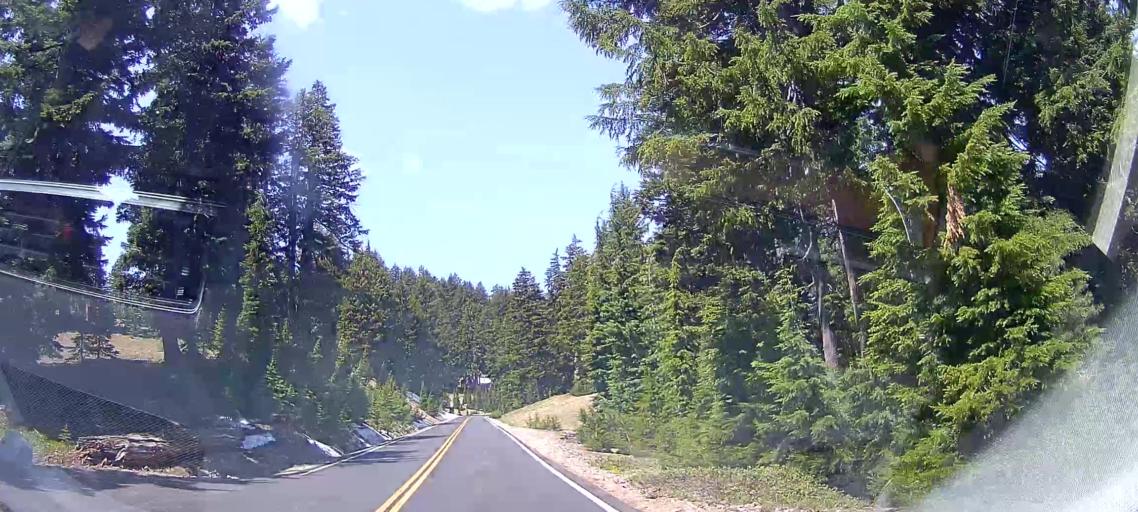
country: US
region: Oregon
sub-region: Jackson County
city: Shady Cove
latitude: 42.9799
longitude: -122.1181
